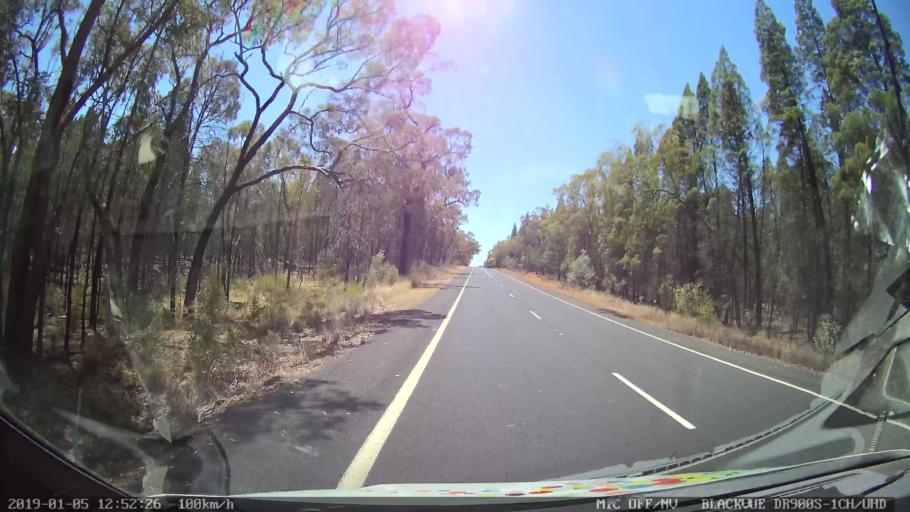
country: AU
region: New South Wales
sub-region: Warrumbungle Shire
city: Coonabarabran
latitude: -31.1211
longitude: 149.6562
